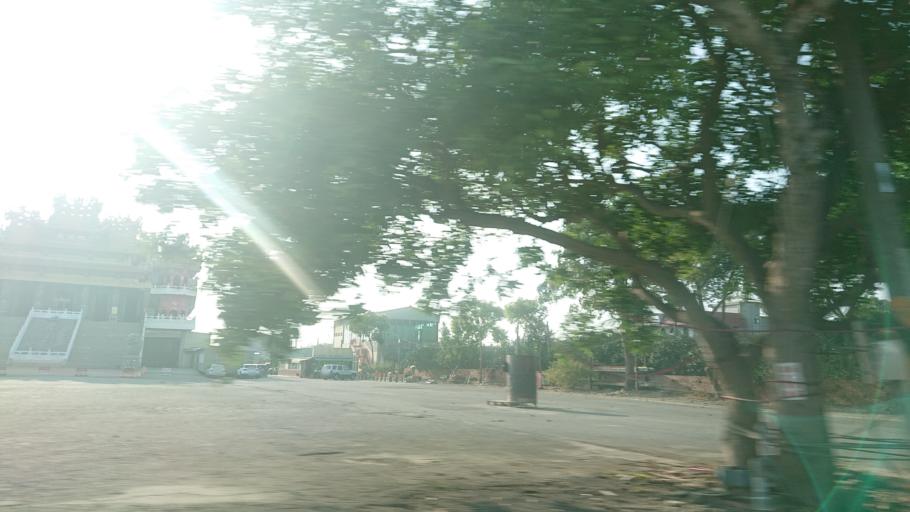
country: TW
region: Taiwan
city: Xinying
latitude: 23.1588
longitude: 120.2500
